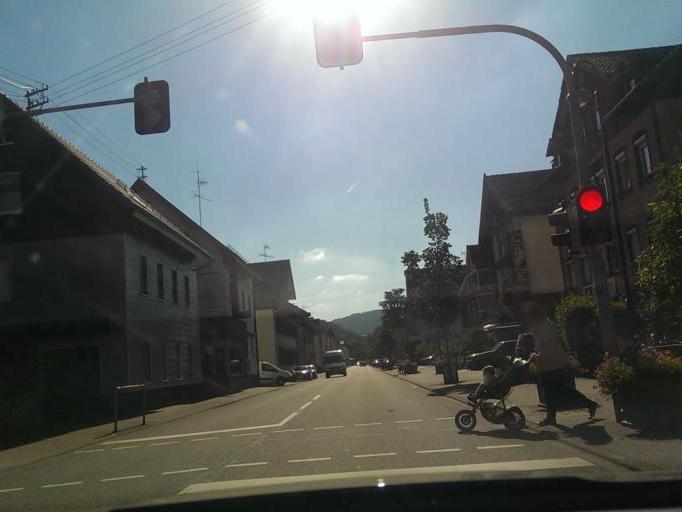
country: DE
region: Baden-Wuerttemberg
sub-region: Karlsruhe Region
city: Hofen an der Enz
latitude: 48.8062
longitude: 8.5838
